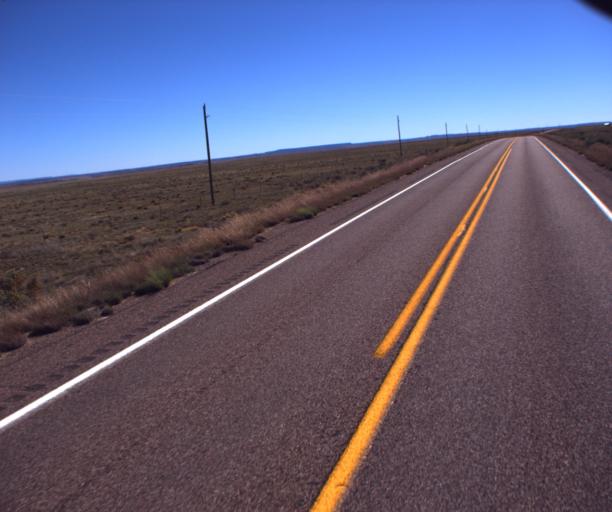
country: US
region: Arizona
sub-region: Apache County
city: Saint Johns
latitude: 34.5409
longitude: -109.4722
